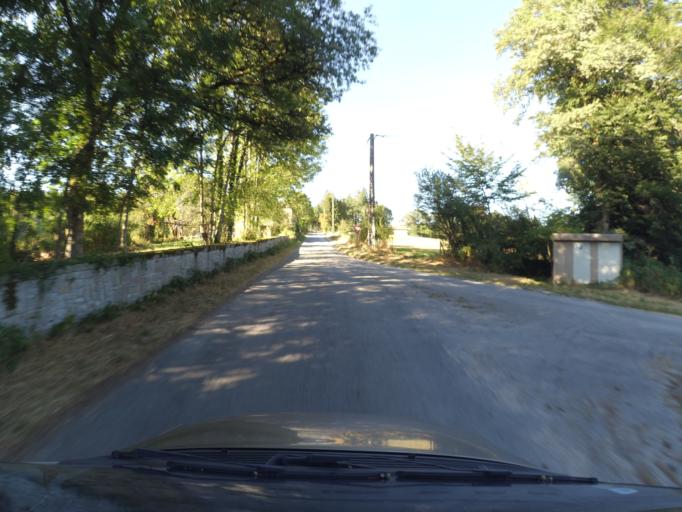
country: FR
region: Limousin
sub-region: Departement de la Creuse
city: Banize
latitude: 45.7951
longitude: 1.9301
